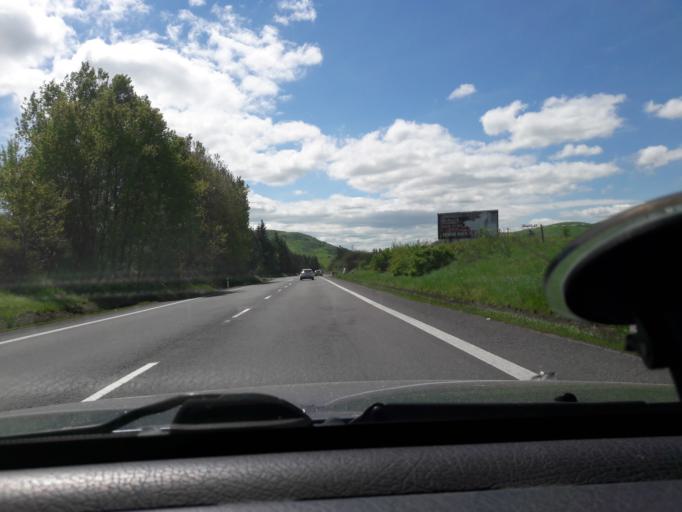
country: SK
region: Banskobystricky
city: Krupina
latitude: 48.4347
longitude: 19.0955
